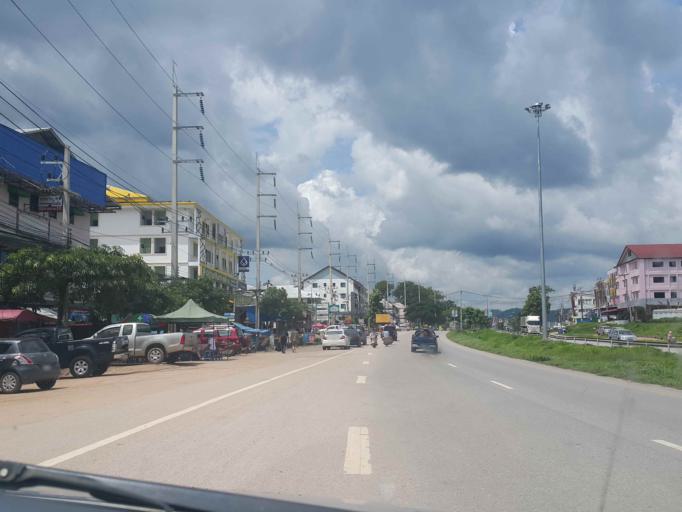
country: TH
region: Phayao
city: Dok Kham Tai
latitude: 19.0299
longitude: 99.9262
